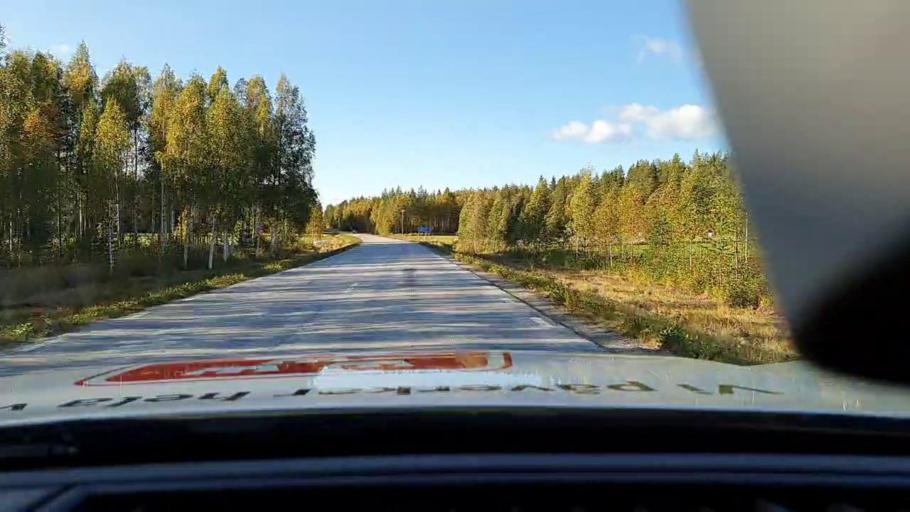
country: SE
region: Norrbotten
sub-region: Pitea Kommun
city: Norrfjarden
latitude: 65.4335
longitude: 21.4853
